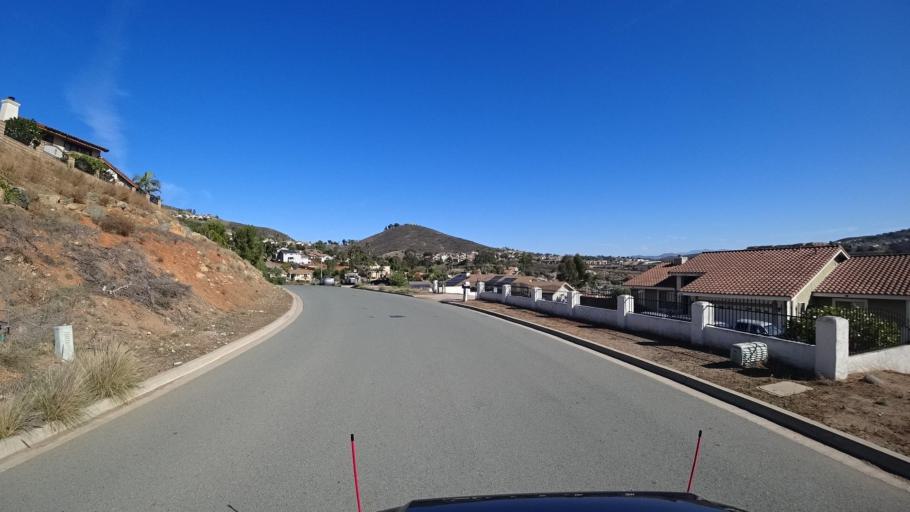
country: US
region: California
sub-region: San Diego County
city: La Presa
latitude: 32.7165
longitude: -116.9802
